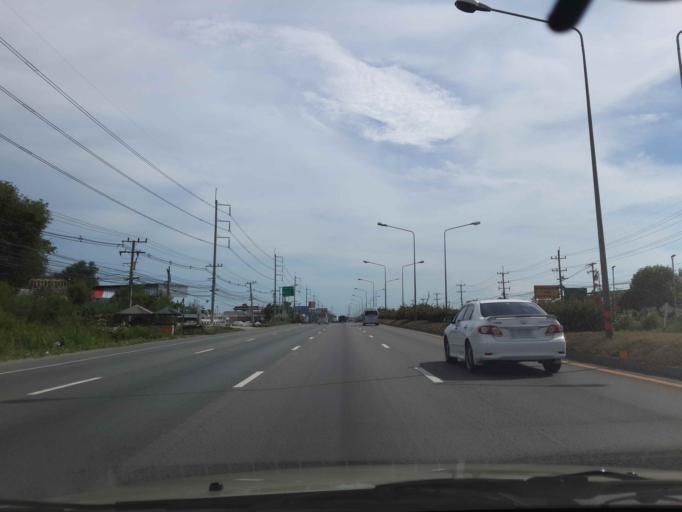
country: TH
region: Chon Buri
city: Chon Buri
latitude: 13.3605
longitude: 101.0143
